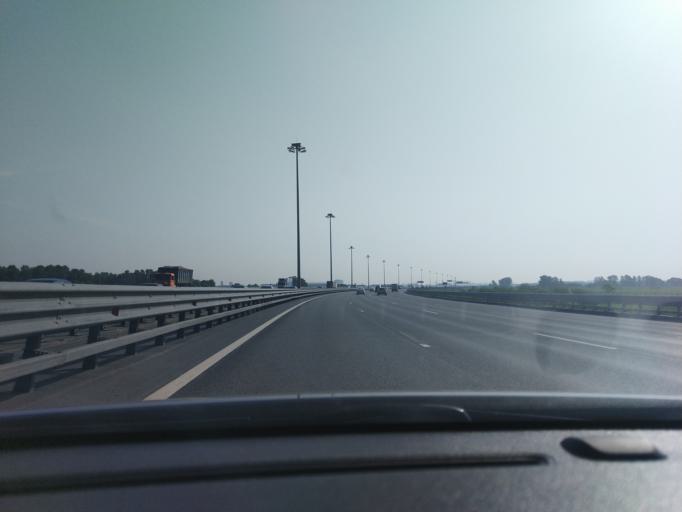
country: RU
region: St.-Petersburg
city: Uritsk
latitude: 59.8089
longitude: 30.1827
